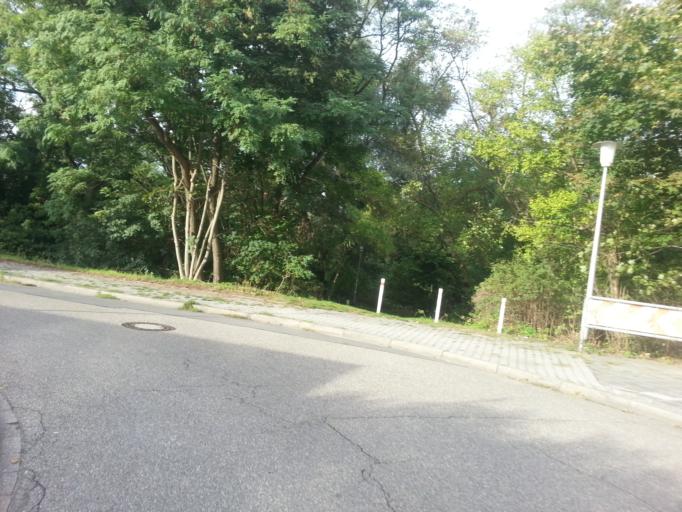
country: DE
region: Rheinland-Pfalz
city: Altrip
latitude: 49.4418
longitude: 8.5225
